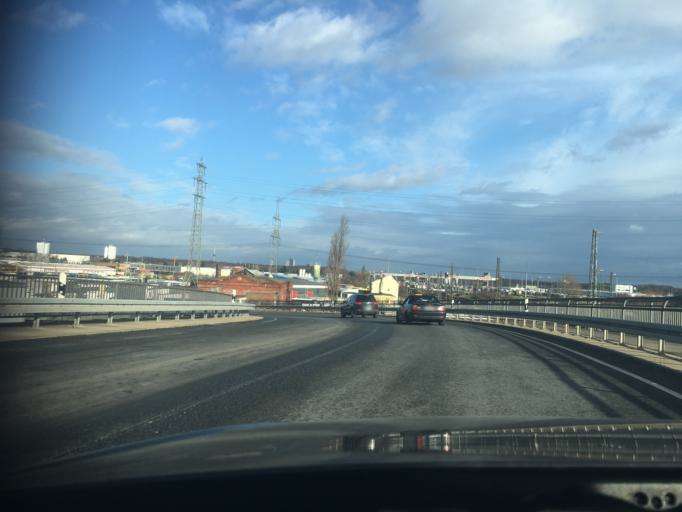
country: DE
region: North Rhine-Westphalia
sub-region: Regierungsbezirk Koln
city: Hurth
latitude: 50.8806
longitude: 6.9109
